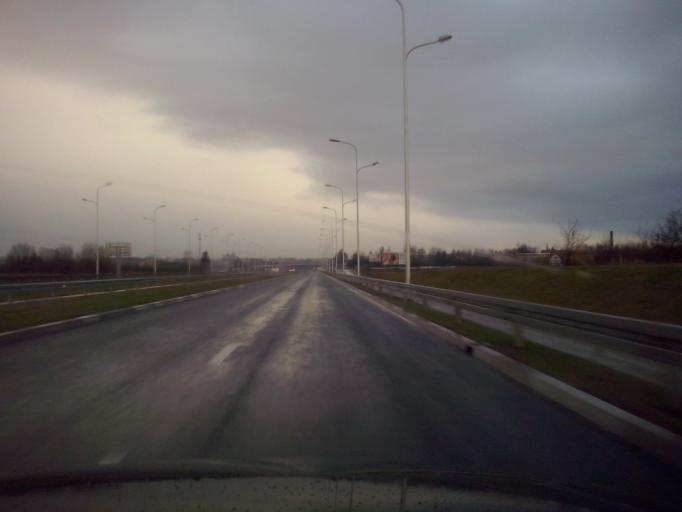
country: PL
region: Lublin Voivodeship
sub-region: Powiat lubelski
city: Jastkow
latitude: 51.2709
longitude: 22.4823
